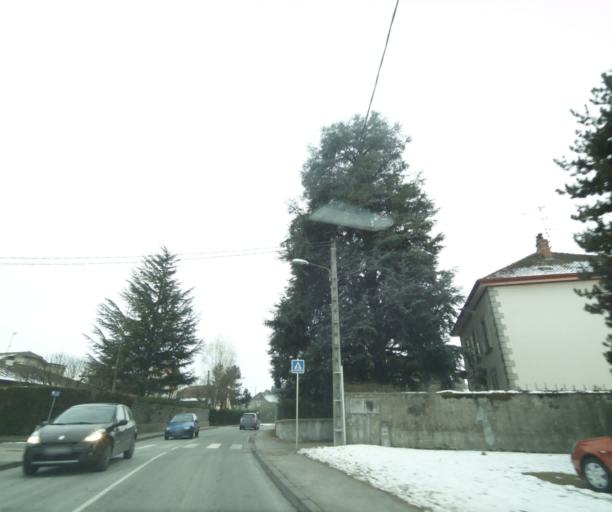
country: FR
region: Rhone-Alpes
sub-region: Departement de la Haute-Savoie
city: Reignier-Esery
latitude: 46.1312
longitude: 6.2677
